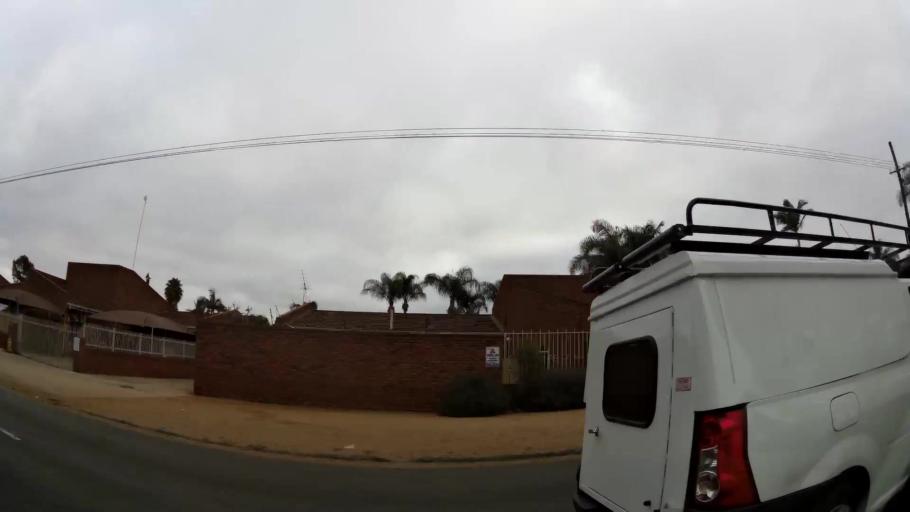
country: ZA
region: Limpopo
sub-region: Capricorn District Municipality
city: Polokwane
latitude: -23.9013
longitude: 29.4573
